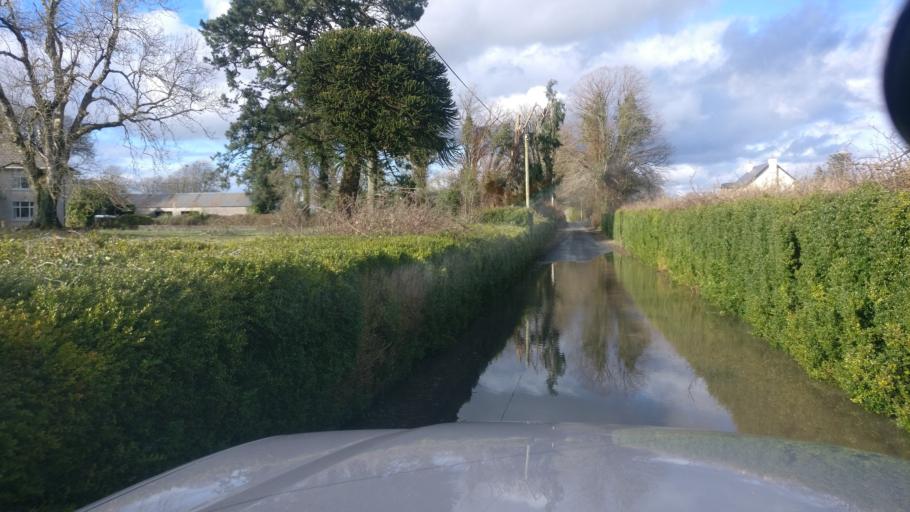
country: IE
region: Connaught
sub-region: County Galway
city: Loughrea
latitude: 53.1785
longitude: -8.4260
